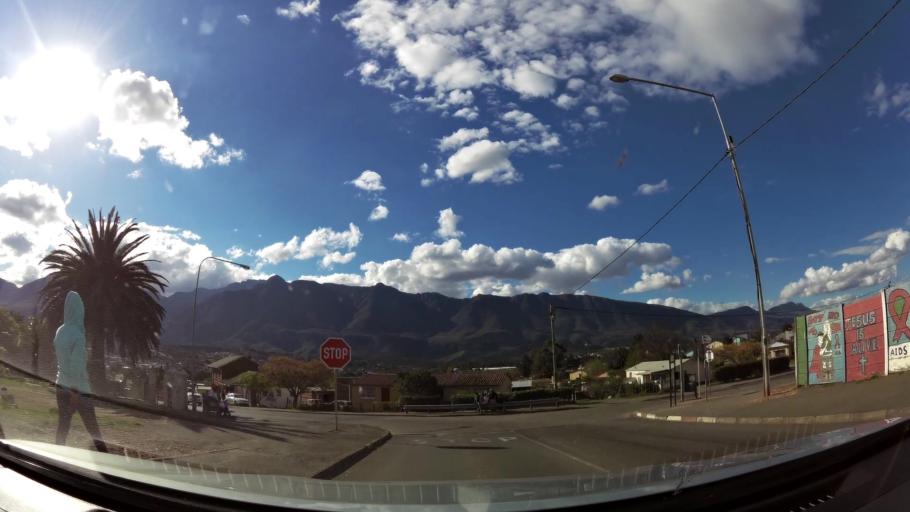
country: ZA
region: Western Cape
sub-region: Overberg District Municipality
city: Swellendam
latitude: -34.0344
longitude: 20.4441
